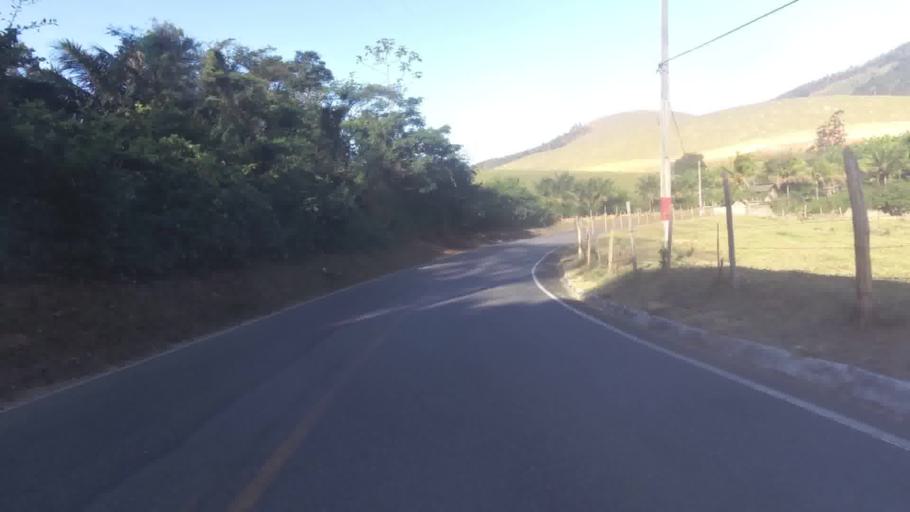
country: BR
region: Espirito Santo
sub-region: Iconha
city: Iconha
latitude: -20.7349
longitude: -40.7636
